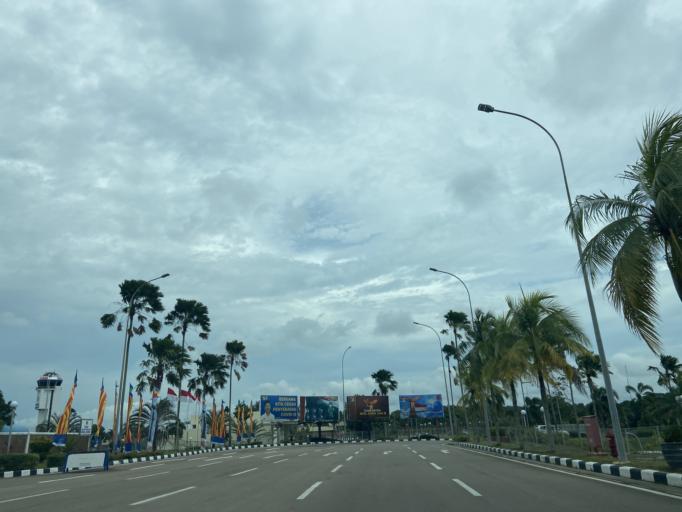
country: SG
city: Singapore
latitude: 1.1225
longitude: 104.1144
